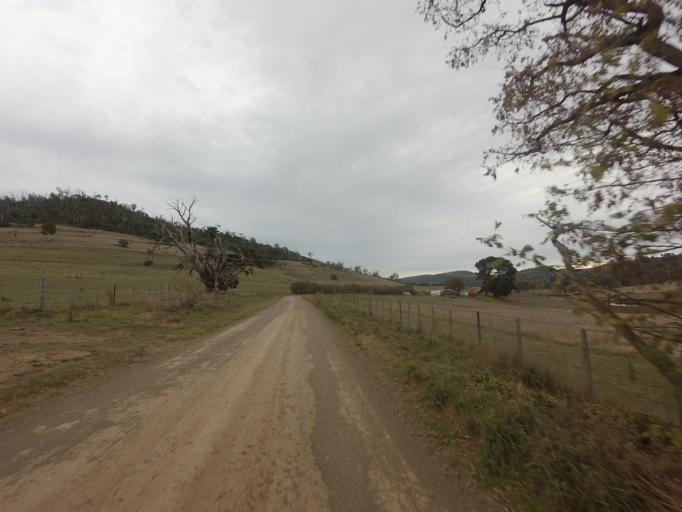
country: AU
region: Tasmania
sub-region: Derwent Valley
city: New Norfolk
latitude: -42.5525
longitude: 146.9595
